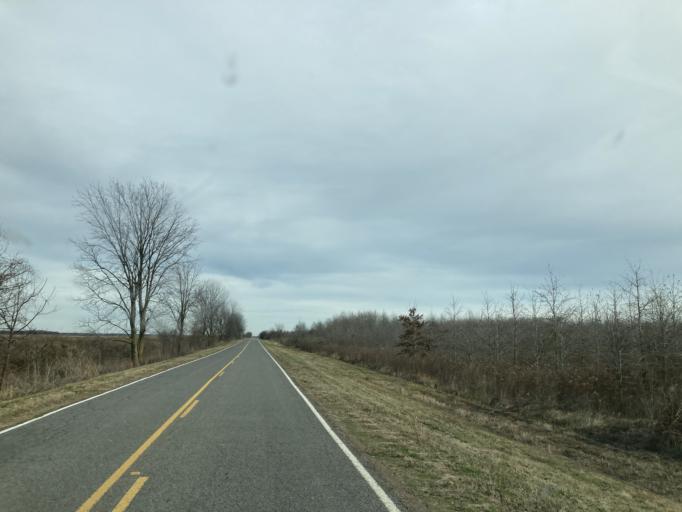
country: US
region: Mississippi
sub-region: Humphreys County
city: Belzoni
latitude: 33.1676
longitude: -90.5713
